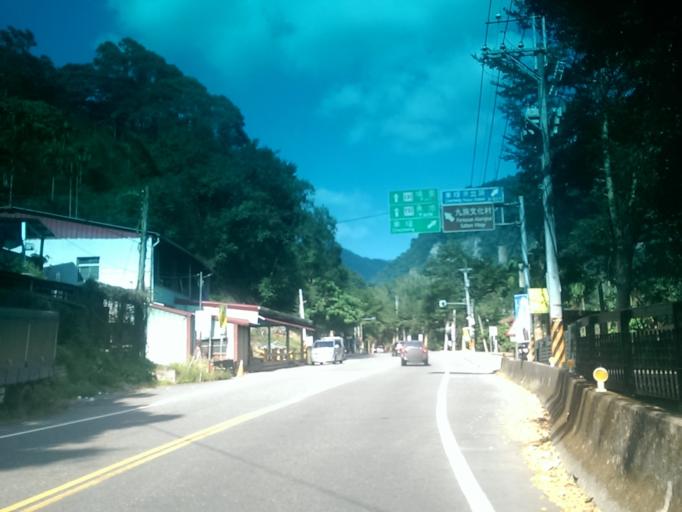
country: TW
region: Taiwan
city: Lugu
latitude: 23.8286
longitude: 120.8625
